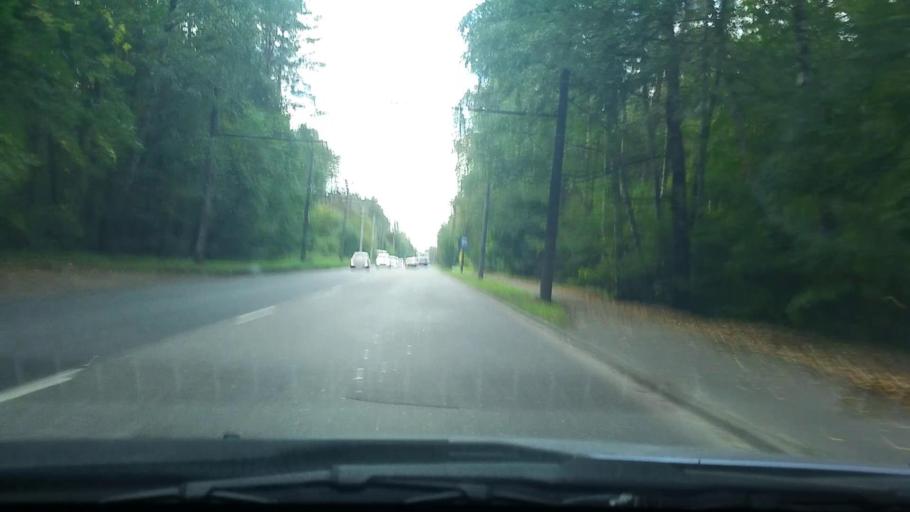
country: LV
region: Riga
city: Jaunciems
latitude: 56.9663
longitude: 24.2033
